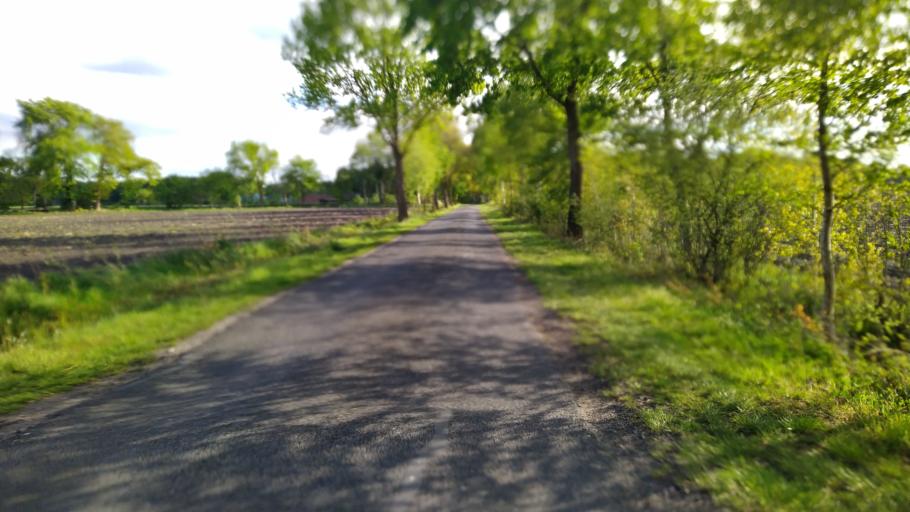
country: DE
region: Lower Saxony
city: Brest
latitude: 53.4061
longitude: 9.3638
